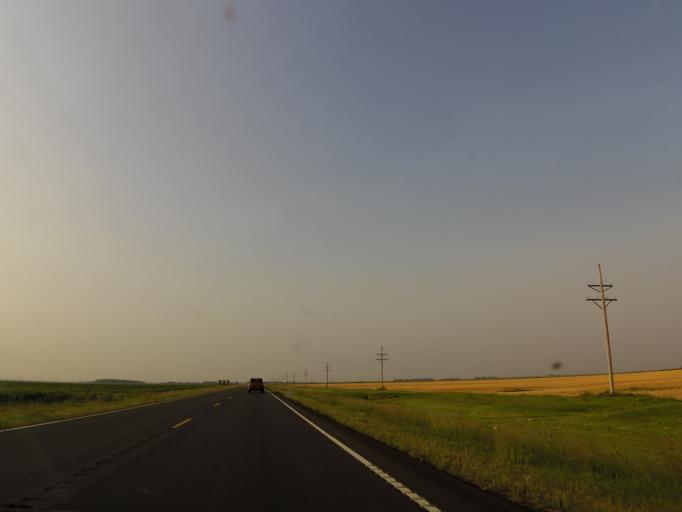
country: US
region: North Dakota
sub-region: Traill County
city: Mayville
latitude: 47.4319
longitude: -97.3260
